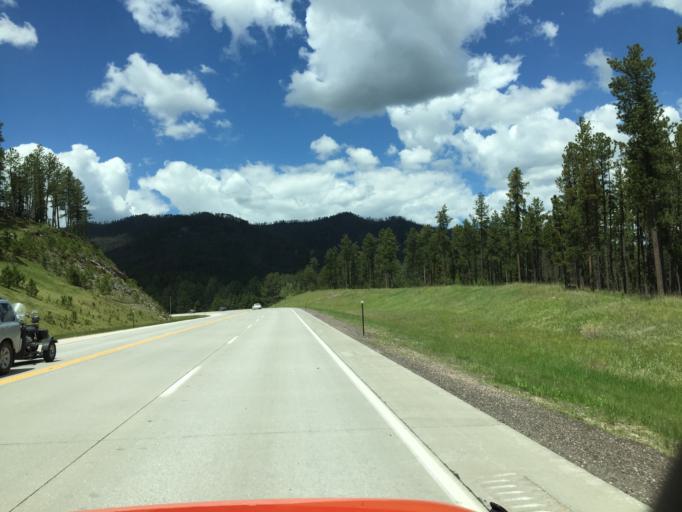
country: US
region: South Dakota
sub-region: Custer County
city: Custer
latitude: 43.8842
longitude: -103.5977
